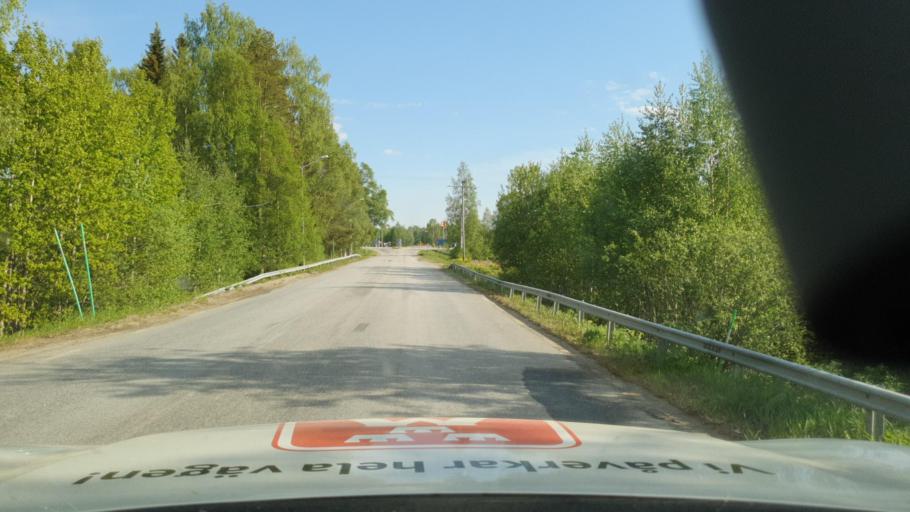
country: SE
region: Vaesterbotten
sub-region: Vannas Kommun
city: Vannasby
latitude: 63.9224
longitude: 19.8436
